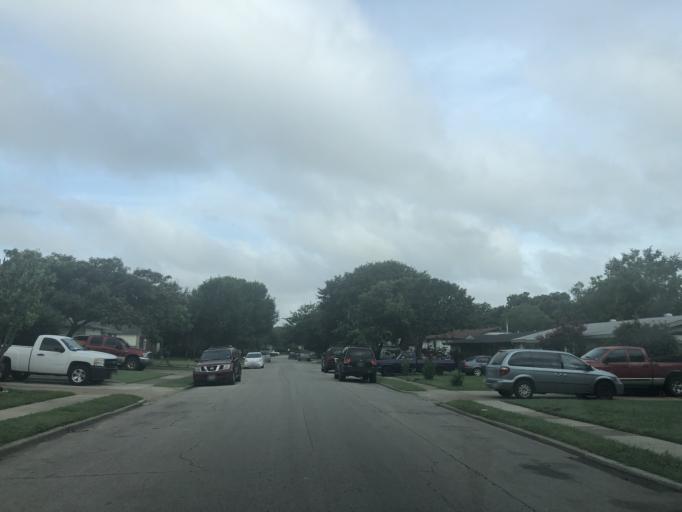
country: US
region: Texas
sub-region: Dallas County
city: Irving
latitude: 32.8120
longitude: -96.9790
